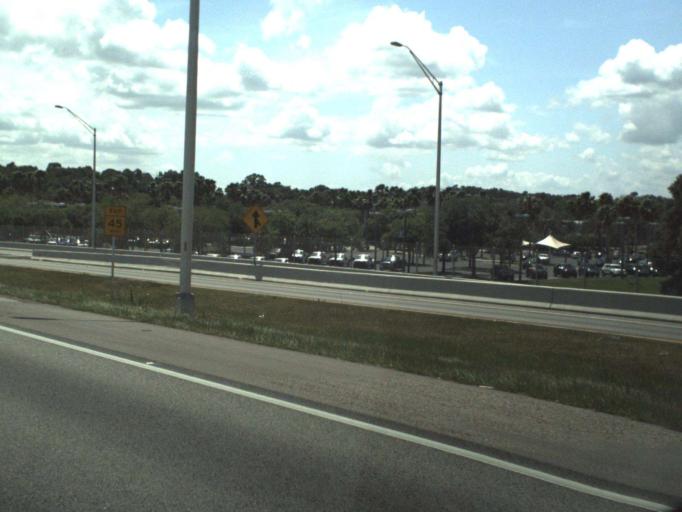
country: US
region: Florida
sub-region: Seminole County
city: Lake Mary
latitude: 28.8096
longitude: -81.3390
